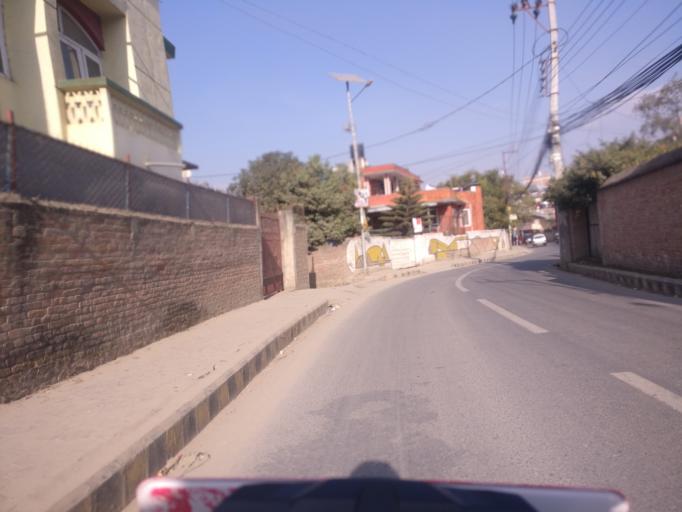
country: NP
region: Central Region
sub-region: Bagmati Zone
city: Patan
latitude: 27.6796
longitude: 85.3225
